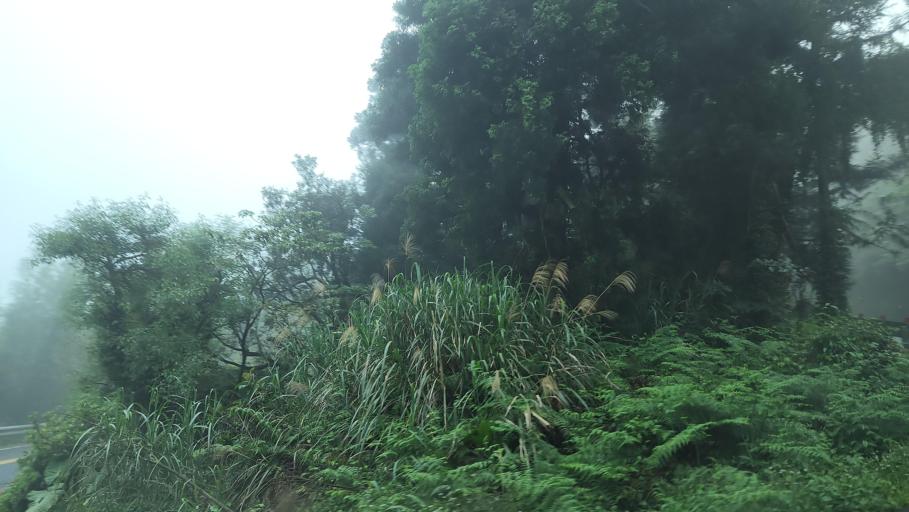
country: TW
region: Taipei
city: Taipei
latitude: 25.1395
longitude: 121.6017
